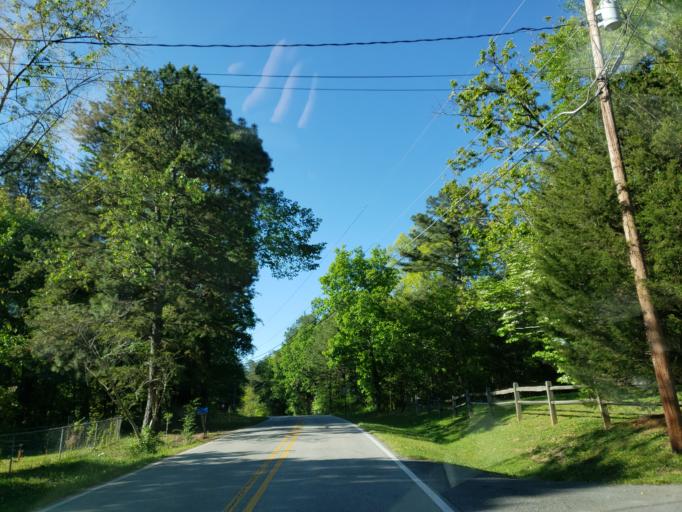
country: US
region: Georgia
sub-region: Polk County
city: Aragon
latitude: 34.0142
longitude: -85.1320
